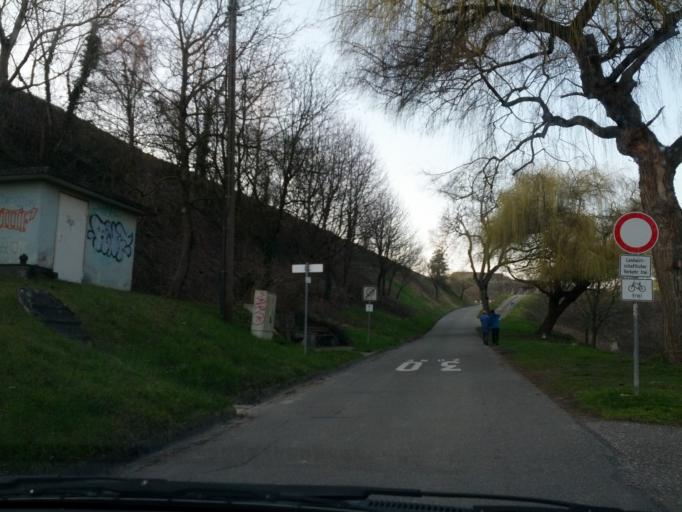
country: DE
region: Baden-Wuerttemberg
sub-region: Freiburg Region
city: Ihringen
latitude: 48.0491
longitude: 7.6459
